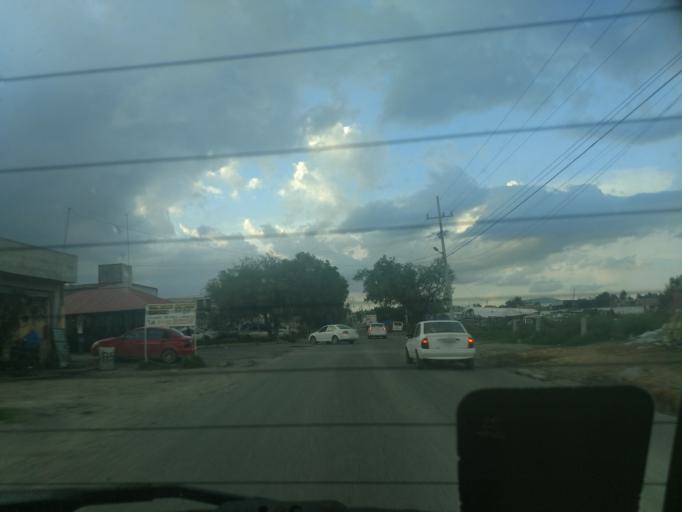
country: MX
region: Morelos
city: Coyotepec
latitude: 19.7590
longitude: -99.2012
